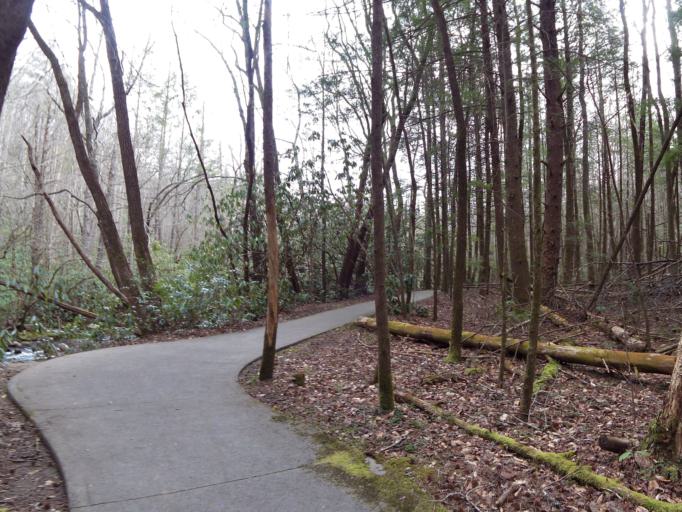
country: US
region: Tennessee
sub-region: Sevier County
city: Gatlinburg
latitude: 35.6780
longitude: -83.5284
